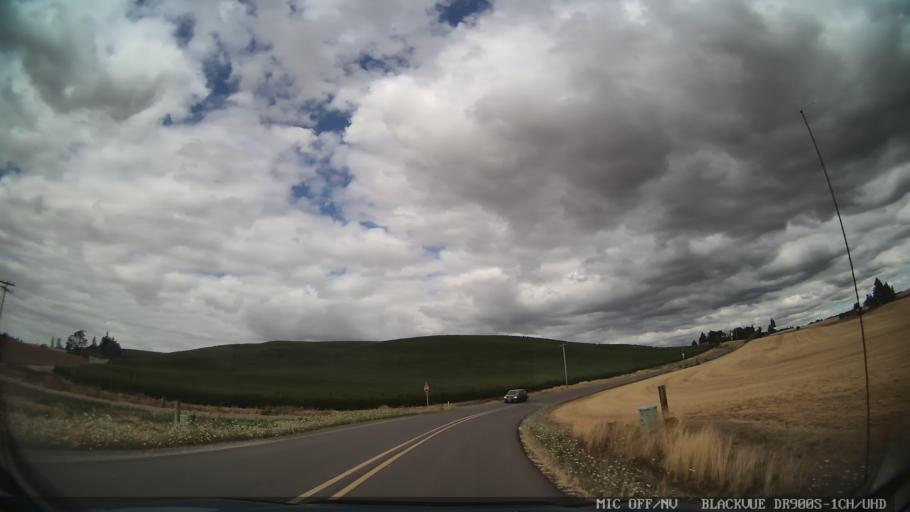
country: US
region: Oregon
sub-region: Marion County
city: Sublimity
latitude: 44.8721
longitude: -122.7342
